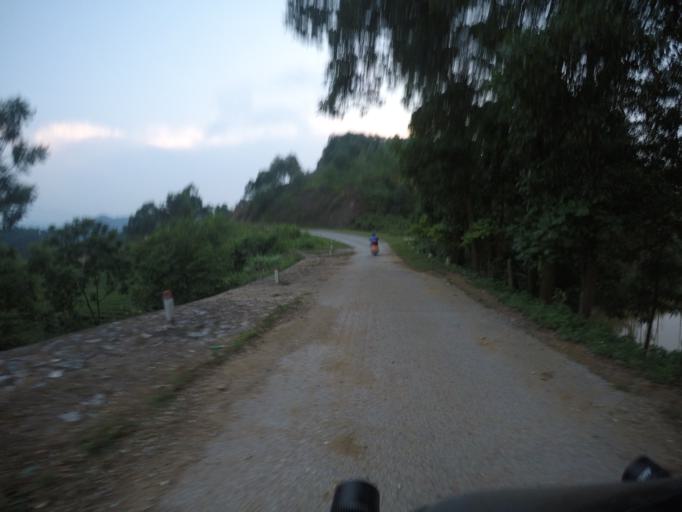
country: VN
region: Thai Nguyen
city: Chua Hang
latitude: 21.5834
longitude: 105.7063
